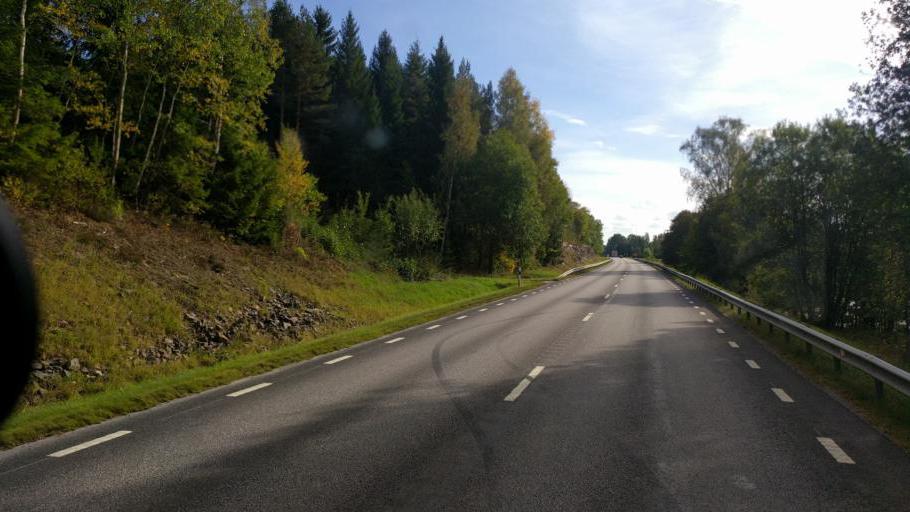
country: SE
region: OEstergoetland
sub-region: Kinda Kommun
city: Kisa
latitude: 57.9332
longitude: 15.6694
